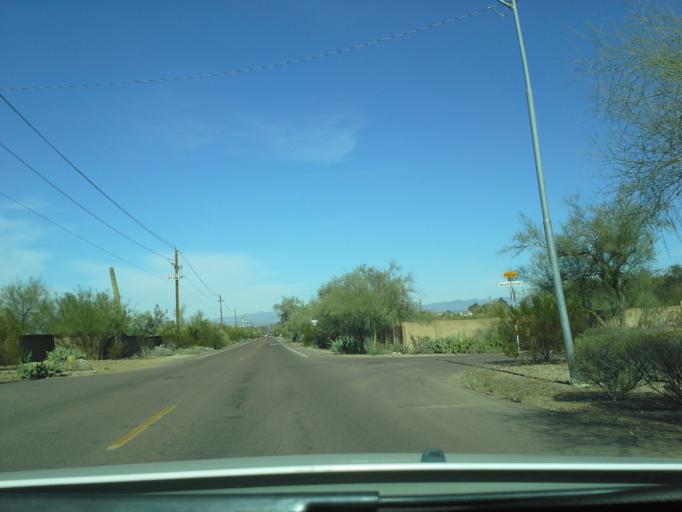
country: US
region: Arizona
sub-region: Maricopa County
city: Paradise Valley
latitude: 33.5752
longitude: -111.9957
